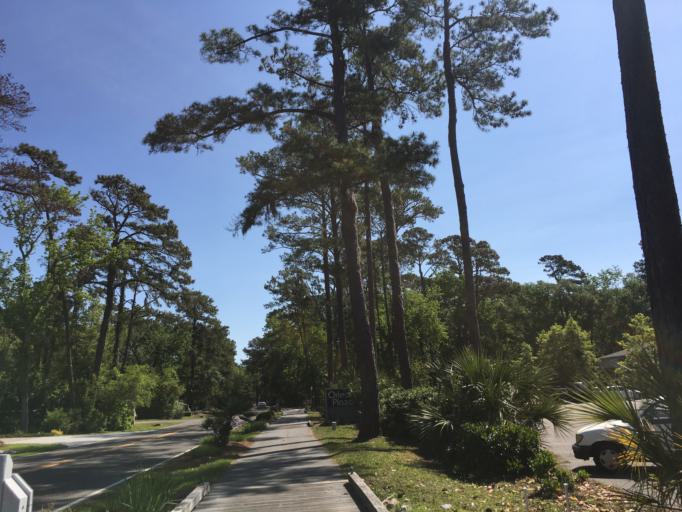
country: US
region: South Carolina
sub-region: Beaufort County
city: Hilton Head Island
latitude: 32.1562
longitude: -80.7573
